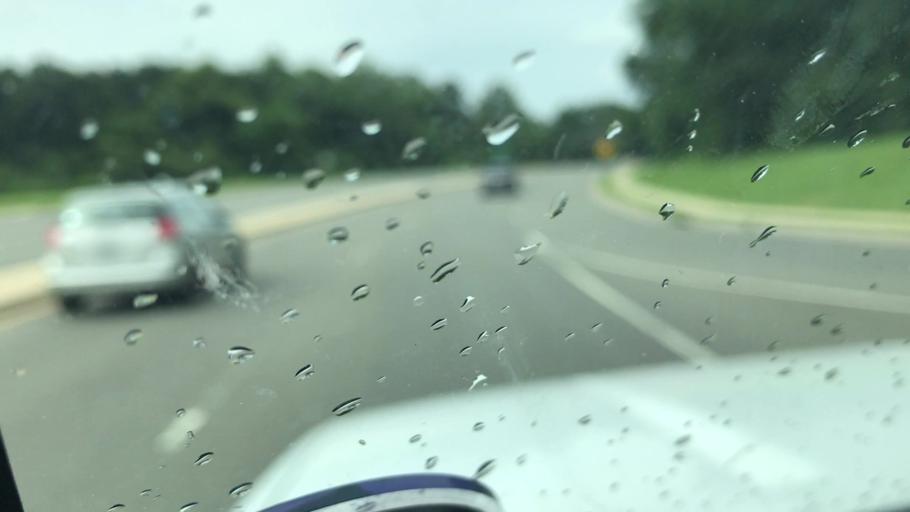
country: US
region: Virginia
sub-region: Henrico County
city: Short Pump
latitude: 37.6337
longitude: -77.6132
